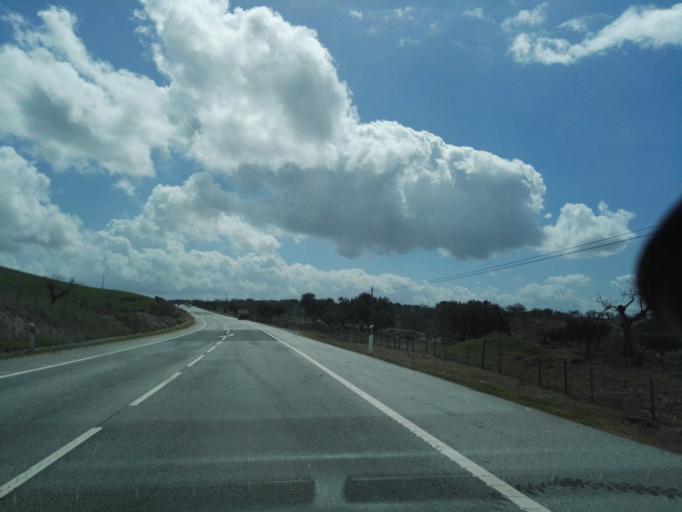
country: PT
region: Portalegre
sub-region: Portalegre
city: Urra
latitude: 39.2525
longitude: -7.4061
